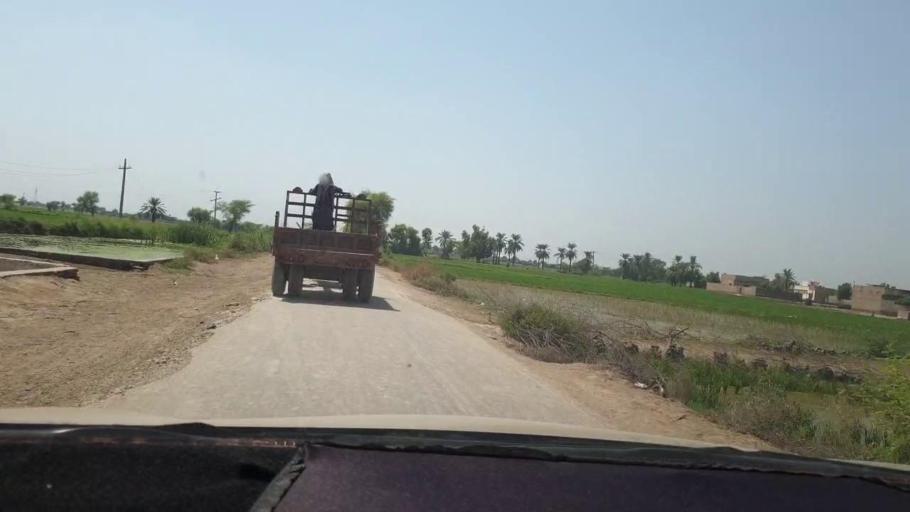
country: PK
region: Sindh
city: Shahdadkot
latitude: 27.8292
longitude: 67.9282
